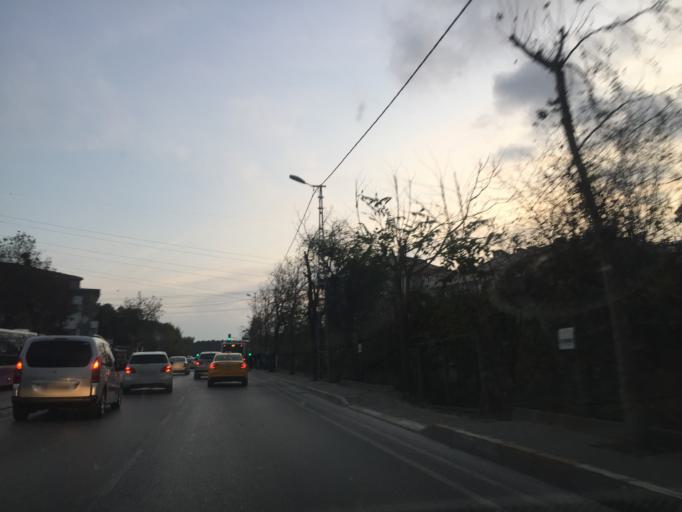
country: TR
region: Istanbul
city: Samandira
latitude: 40.9766
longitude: 29.2197
